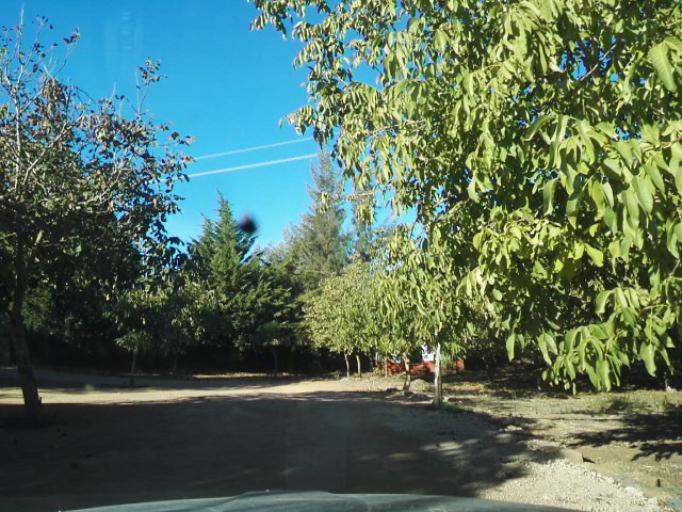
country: PT
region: Portalegre
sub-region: Elvas
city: Elvas
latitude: 38.9214
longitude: -7.1721
